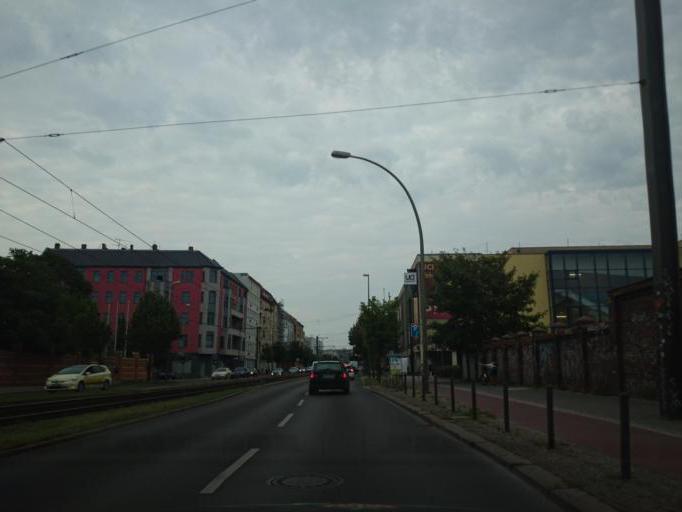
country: DE
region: Berlin
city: Friedrichshain Bezirk
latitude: 52.5244
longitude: 13.4415
